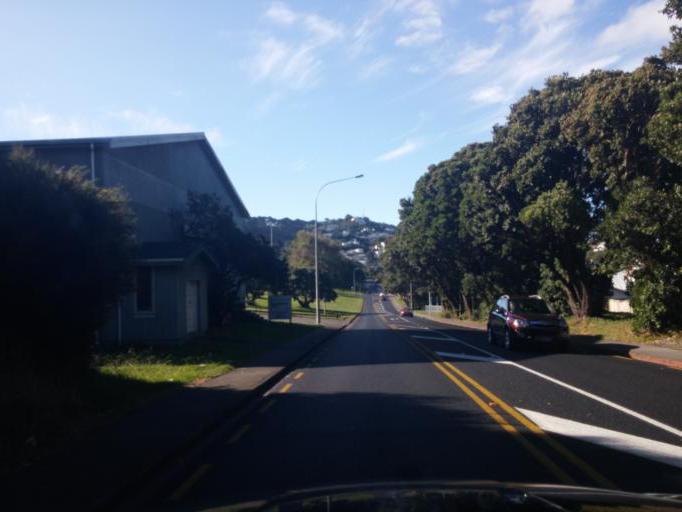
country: NZ
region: Wellington
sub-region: Wellington City
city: Wellington
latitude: -41.3106
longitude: 174.7907
